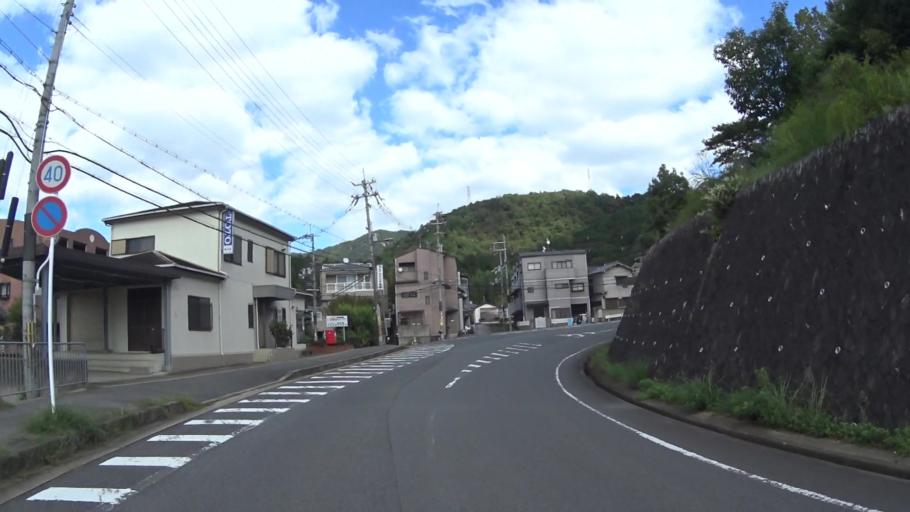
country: JP
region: Kyoto
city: Uji
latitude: 34.9290
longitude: 135.8148
